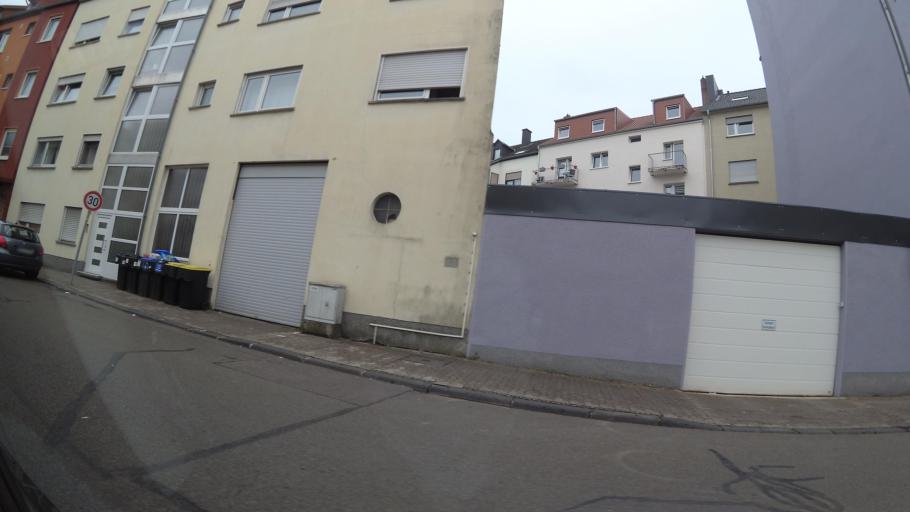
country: DE
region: Saarland
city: Saarbrucken
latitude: 49.2424
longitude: 6.9495
